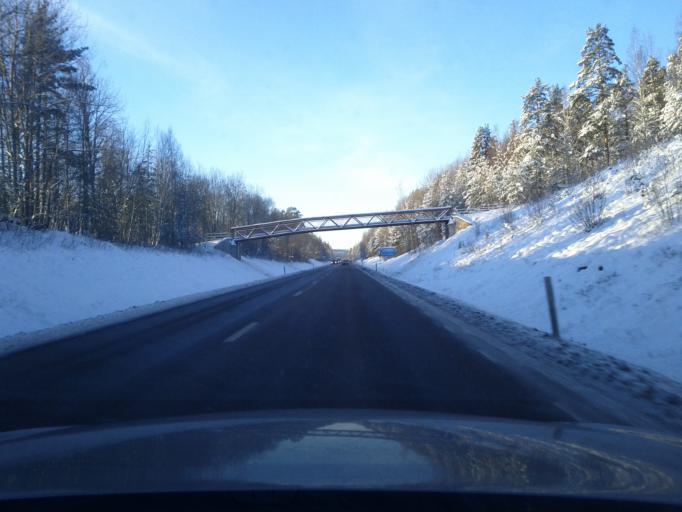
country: SE
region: Dalarna
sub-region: Faluns Kommun
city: Falun
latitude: 60.6253
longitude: 15.6364
